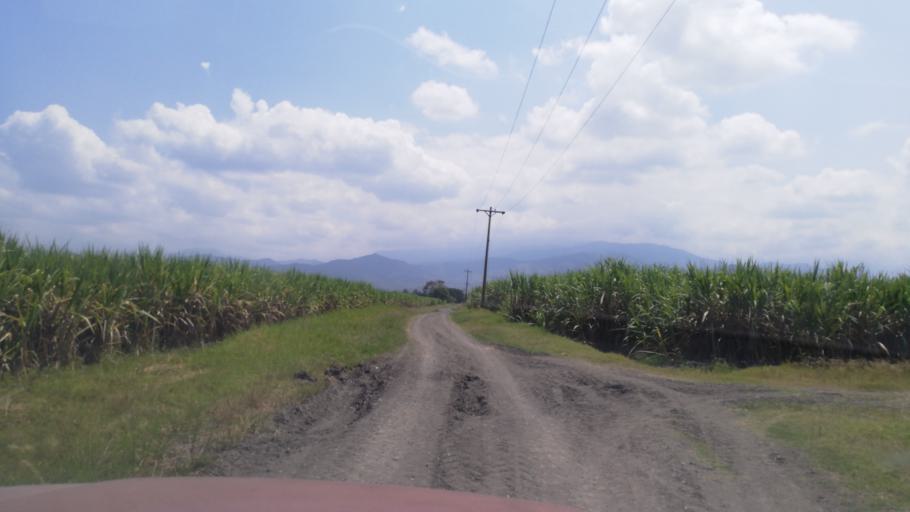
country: CO
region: Valle del Cauca
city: San Pedro
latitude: 3.9950
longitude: -76.2707
